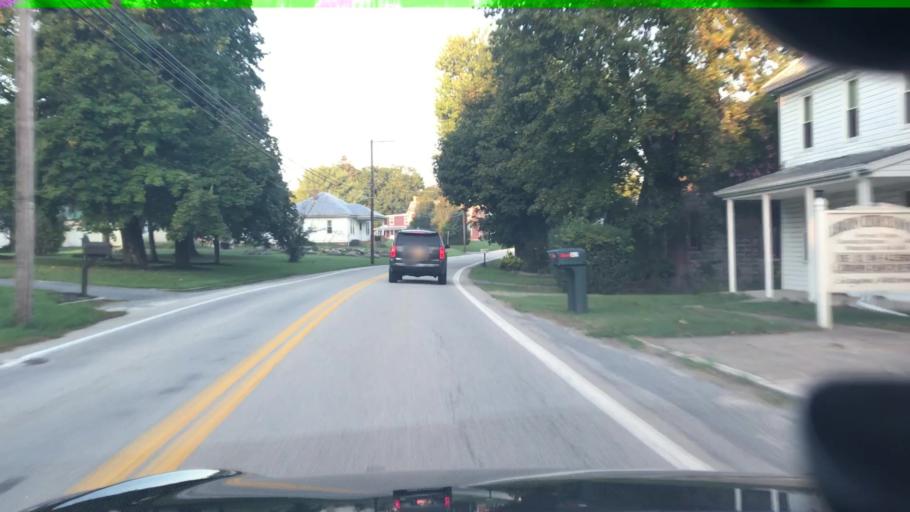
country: US
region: Pennsylvania
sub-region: Cumberland County
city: Lower Allen
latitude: 40.1677
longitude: -76.9141
